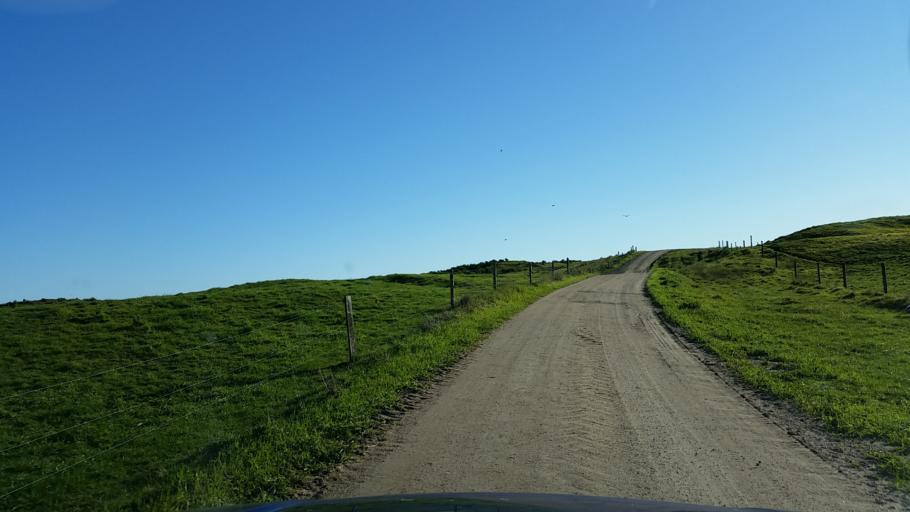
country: NZ
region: Taranaki
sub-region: South Taranaki District
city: Patea
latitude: -39.8378
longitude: 174.6953
